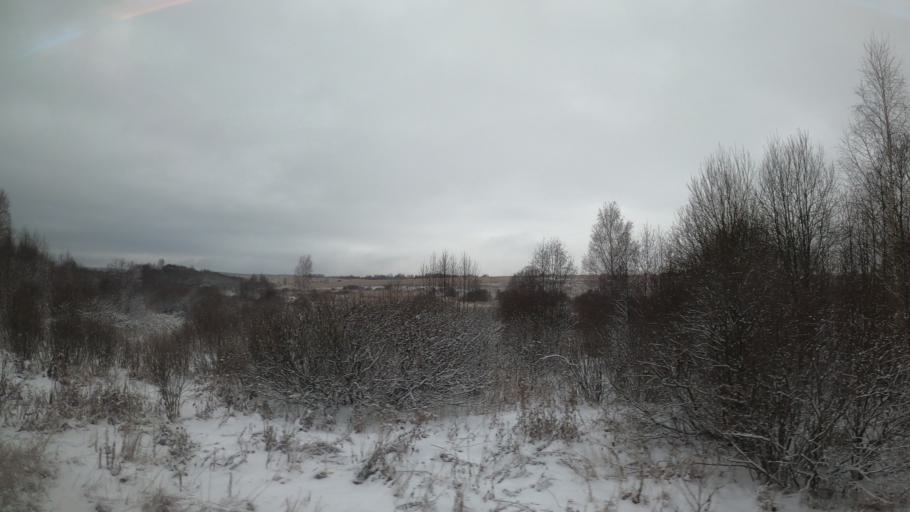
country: RU
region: Jaroslavl
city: Pereslavl'-Zalesskiy
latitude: 56.6930
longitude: 38.9155
